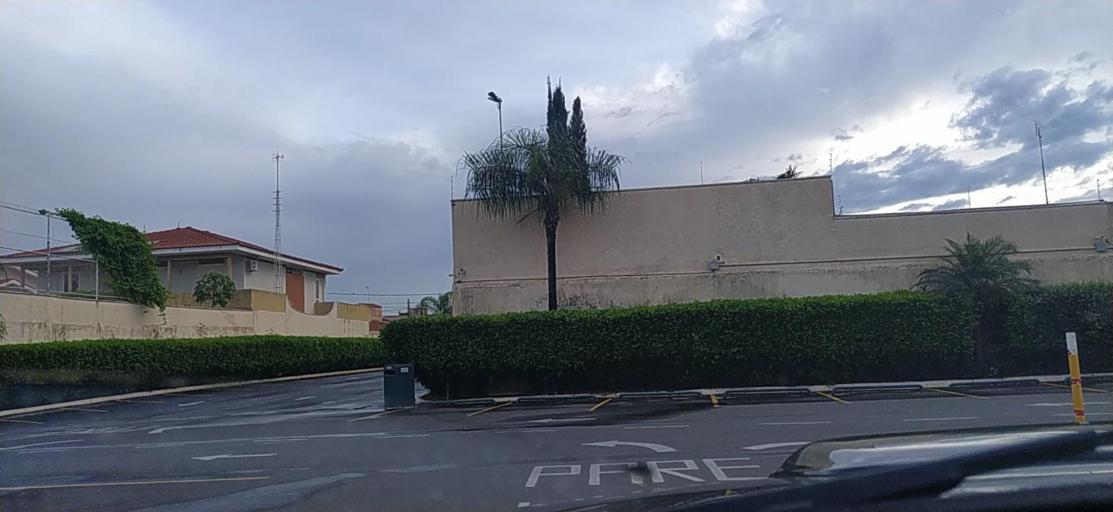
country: BR
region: Sao Paulo
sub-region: Catanduva
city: Catanduva
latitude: -21.1371
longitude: -48.9679
